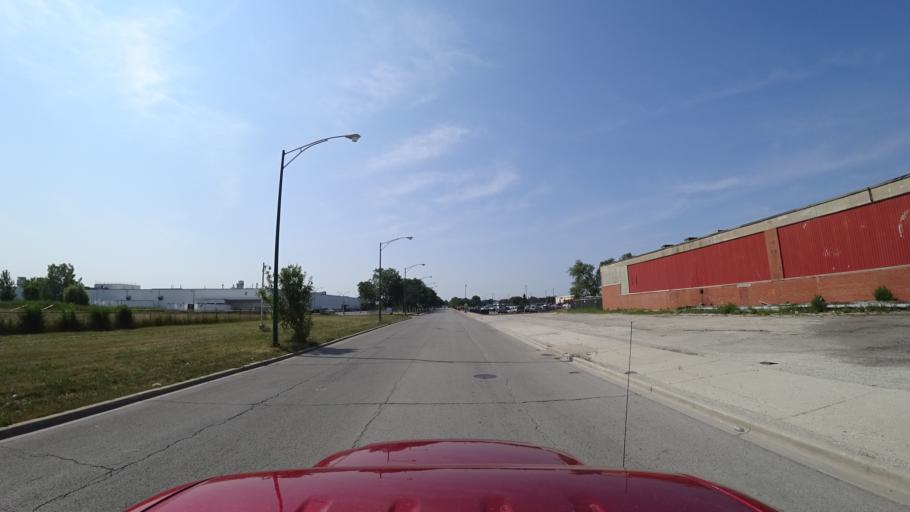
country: US
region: Illinois
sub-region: Cook County
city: Hometown
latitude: 41.7596
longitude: -87.7326
